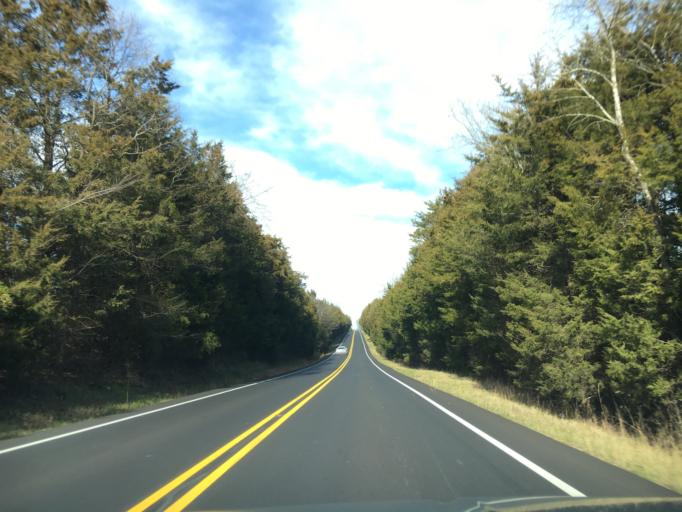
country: US
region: Virginia
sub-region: Orange County
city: Orange
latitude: 38.1986
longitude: -77.9425
